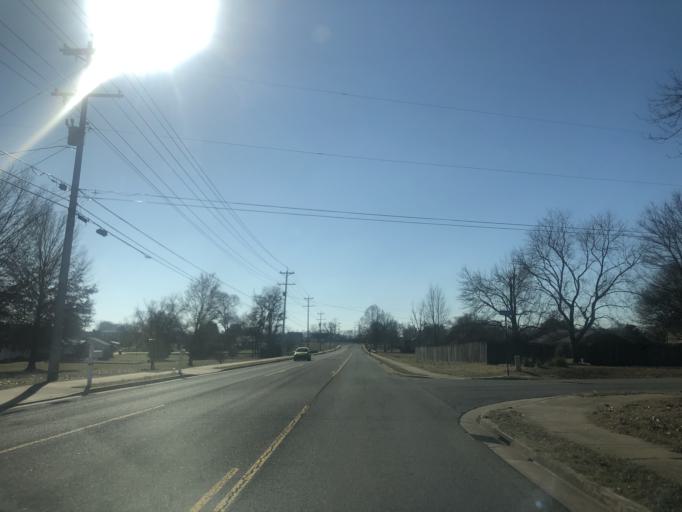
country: US
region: Tennessee
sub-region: Rutherford County
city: Smyrna
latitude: 35.9016
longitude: -86.4754
